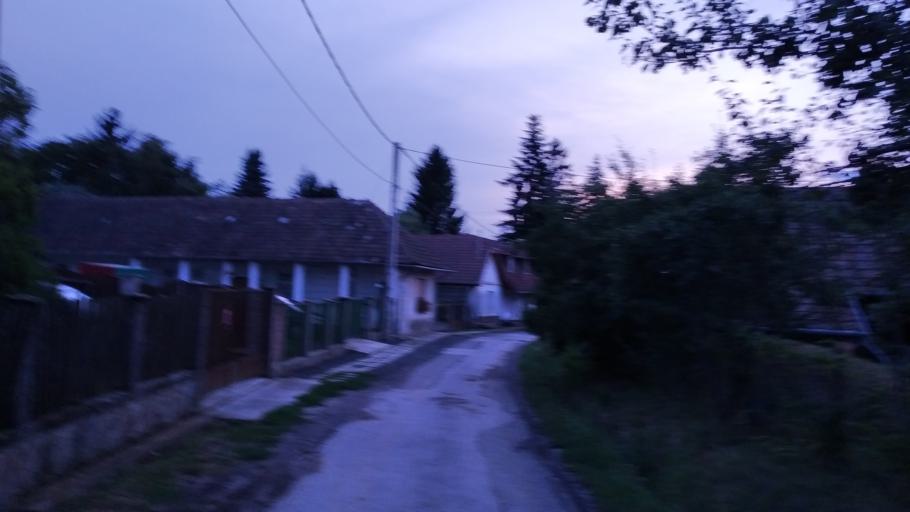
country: HU
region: Pest
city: Szob
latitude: 47.9351
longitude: 18.8304
